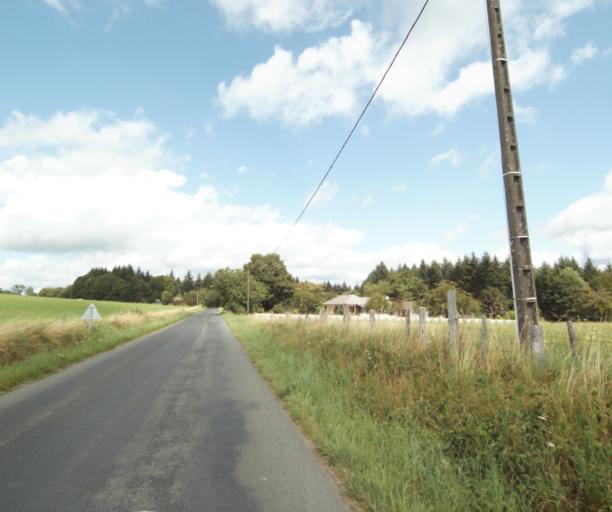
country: FR
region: Limousin
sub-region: Departement de la Correze
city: Sainte-Fortunade
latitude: 45.1905
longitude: 1.8142
